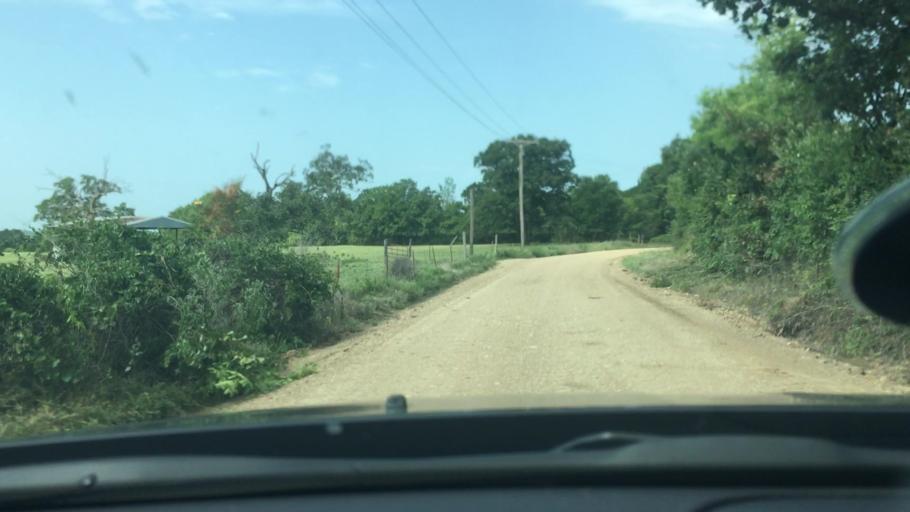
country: US
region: Oklahoma
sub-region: Atoka County
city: Atoka
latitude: 34.4411
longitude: -96.0567
